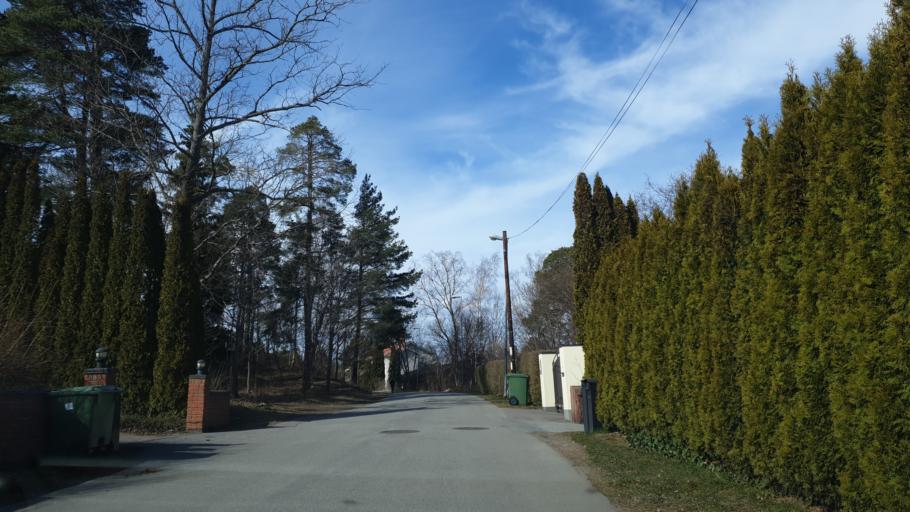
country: SE
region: Stockholm
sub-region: Sollentuna Kommun
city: Sollentuna
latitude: 59.4182
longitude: 17.9838
